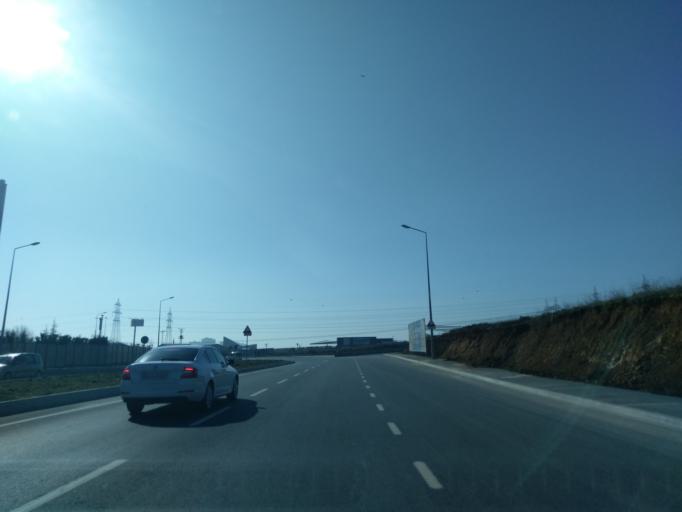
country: TR
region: Istanbul
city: Basaksehir
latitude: 41.1201
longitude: 28.7981
